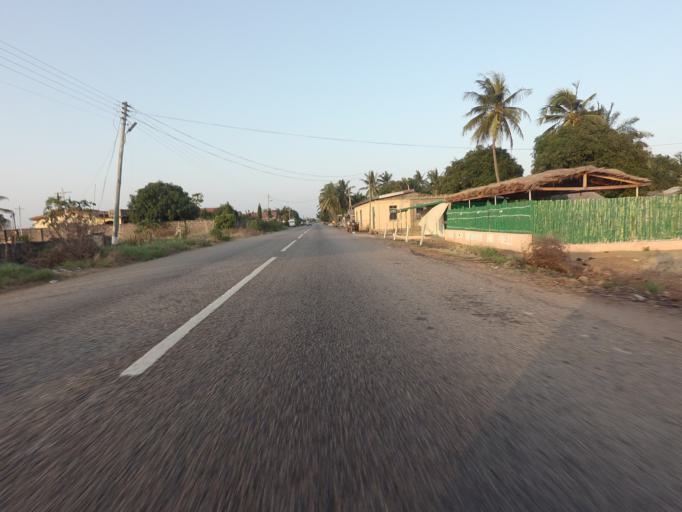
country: GH
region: Volta
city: Anloga
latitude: 5.7832
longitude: 0.8463
